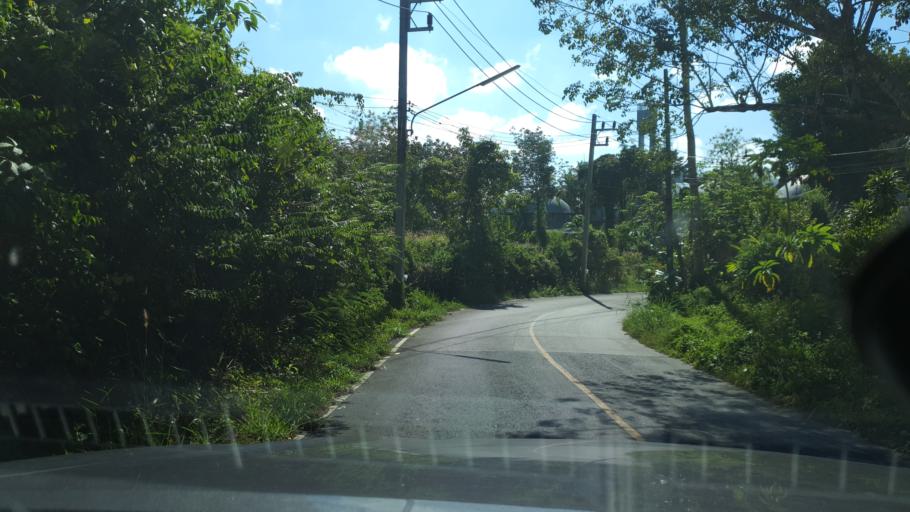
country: TH
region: Phangnga
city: Ban Ao Nang
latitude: 8.0261
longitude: 98.8551
